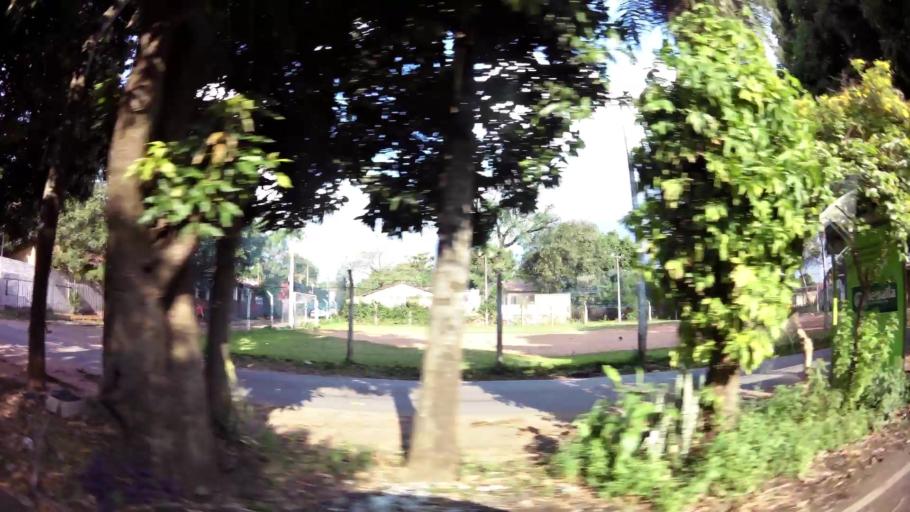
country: PY
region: Central
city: Fernando de la Mora
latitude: -25.3525
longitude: -57.5537
